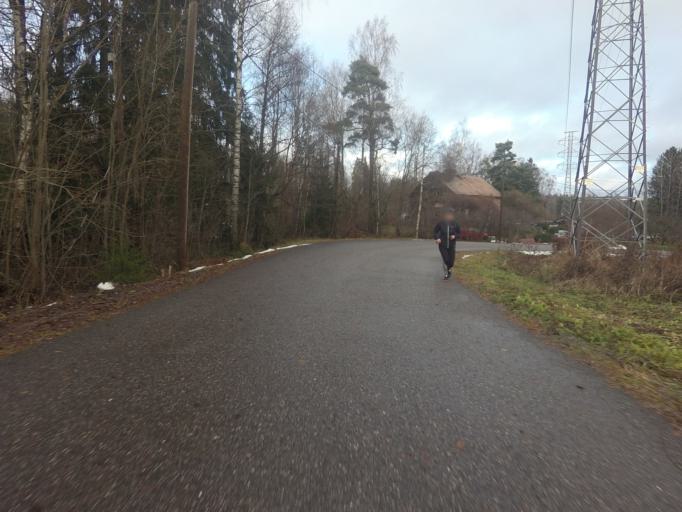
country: FI
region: Uusimaa
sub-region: Helsinki
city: Otaniemi
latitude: 60.1974
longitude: 24.8074
